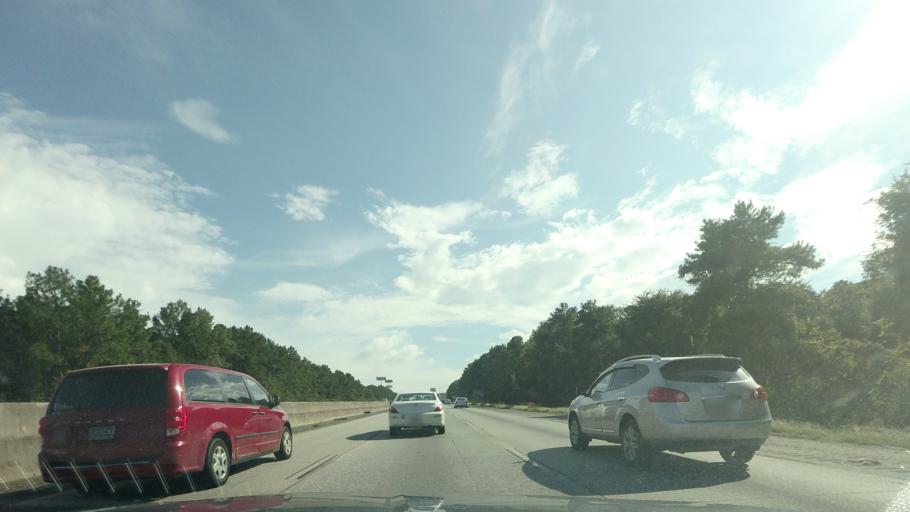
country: US
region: Georgia
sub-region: Peach County
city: Byron
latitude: 32.6841
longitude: -83.7414
